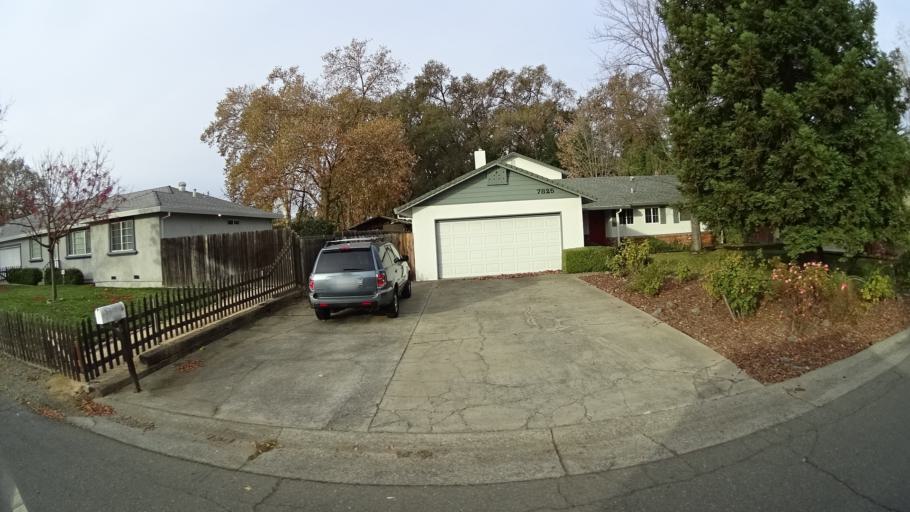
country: US
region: California
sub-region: Sacramento County
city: Citrus Heights
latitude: 38.7084
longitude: -121.2782
